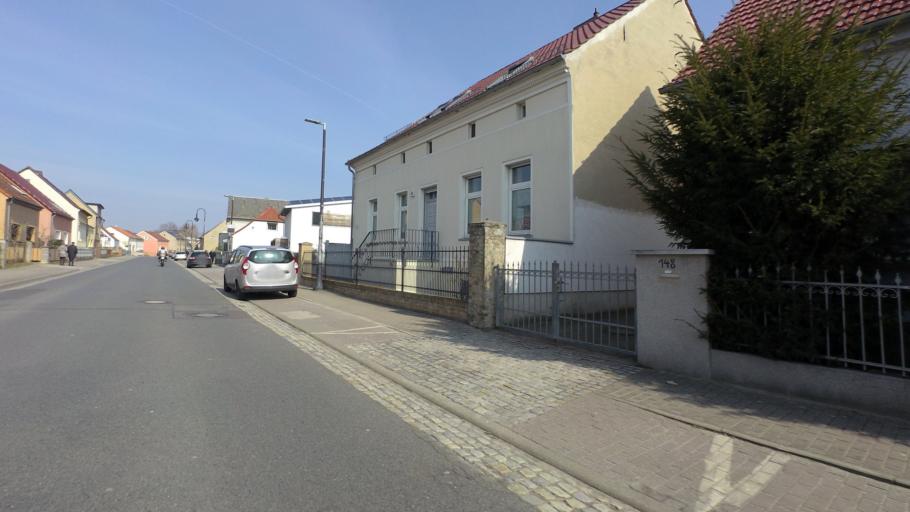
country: DE
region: Brandenburg
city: Werder
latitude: 52.3732
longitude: 12.9359
